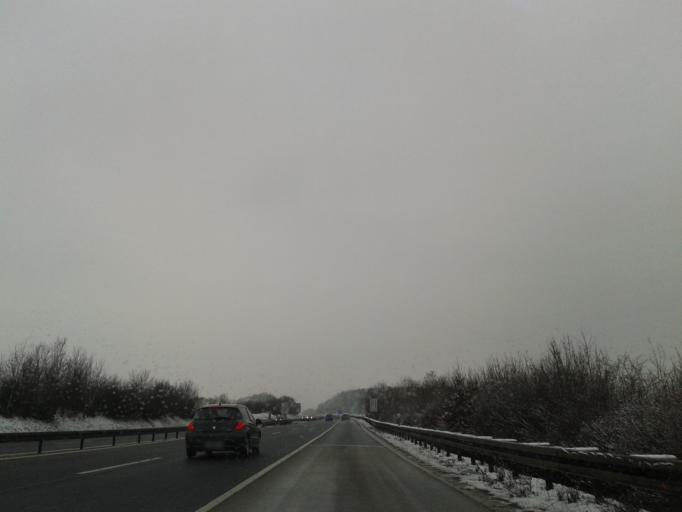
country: DE
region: Bavaria
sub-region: Regierungsbezirk Unterfranken
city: Gadheim
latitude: 50.0220
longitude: 10.3231
